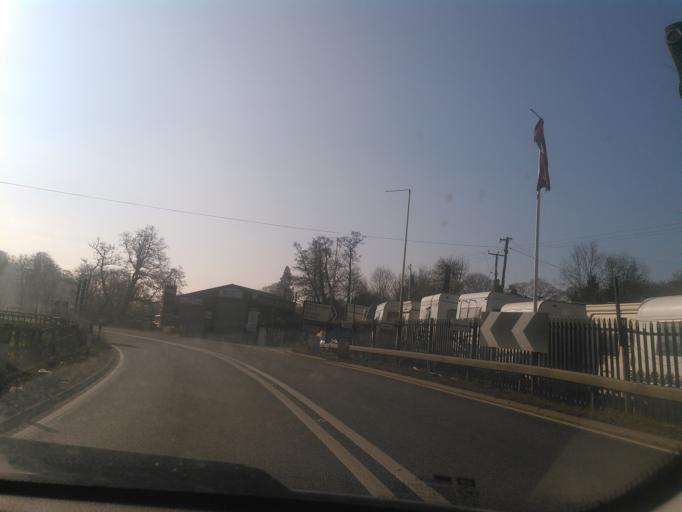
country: GB
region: England
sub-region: Shropshire
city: Church Stretton
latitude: 52.5044
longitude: -2.8233
